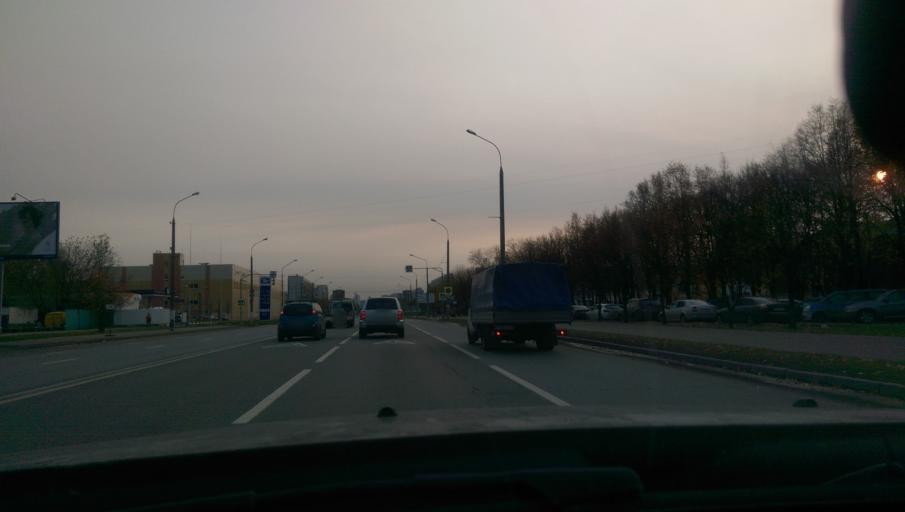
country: RU
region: Moscow
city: Vatutino
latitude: 55.8795
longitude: 37.6695
